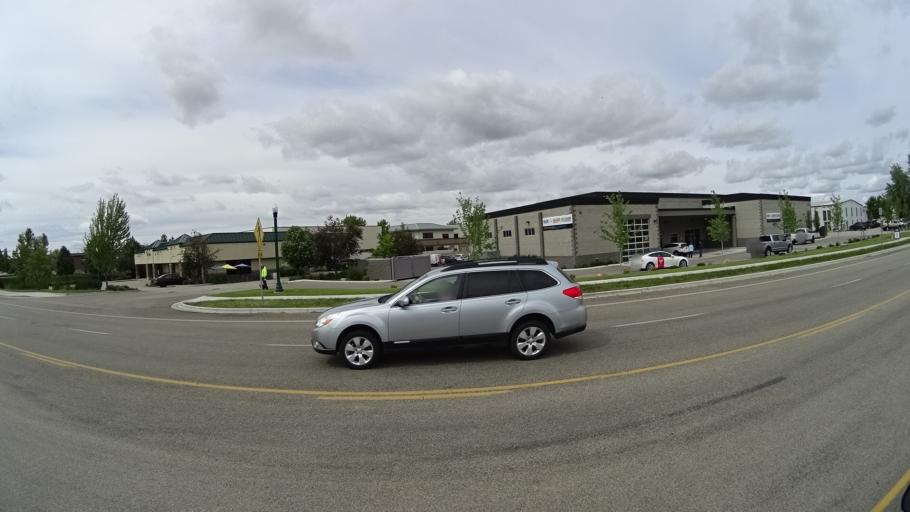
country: US
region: Idaho
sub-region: Ada County
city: Eagle
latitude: 43.6905
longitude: -116.3344
